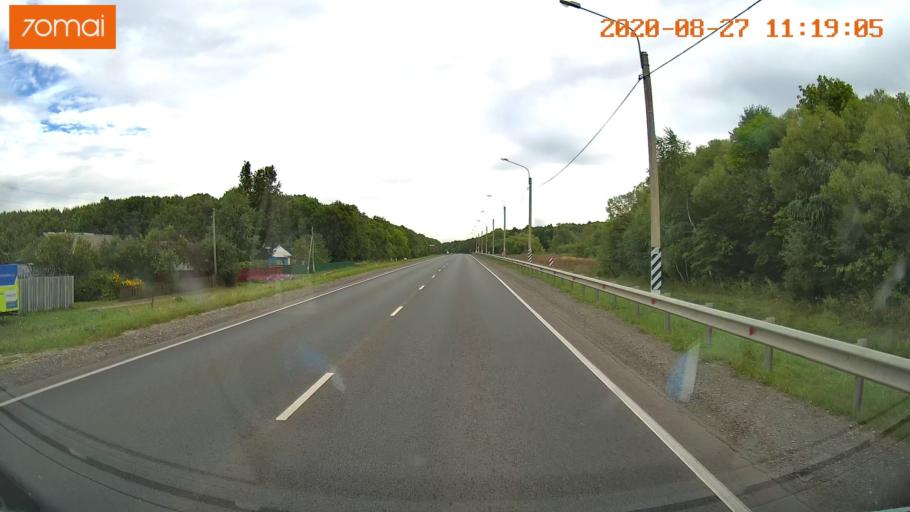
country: RU
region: Rjazan
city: Oktyabr'skiy
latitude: 54.1819
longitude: 38.9091
